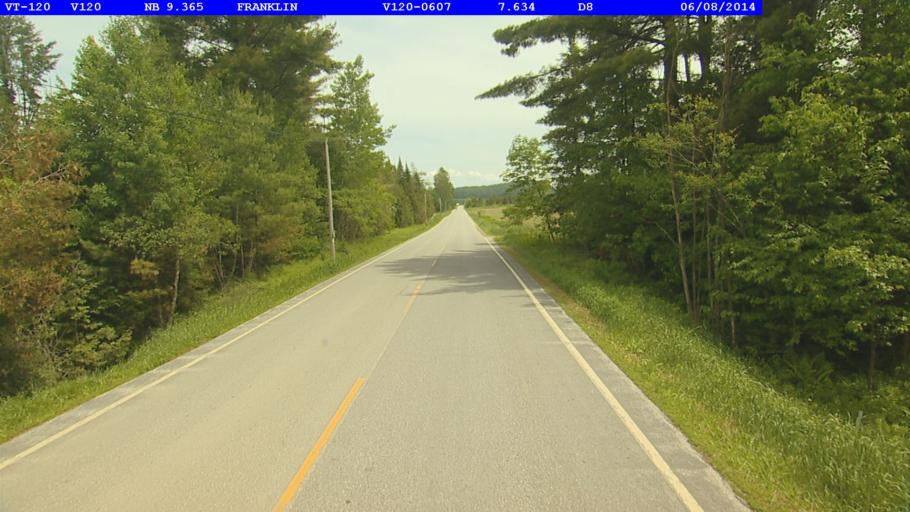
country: US
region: Vermont
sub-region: Franklin County
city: Enosburg Falls
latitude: 44.9910
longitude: -72.8438
